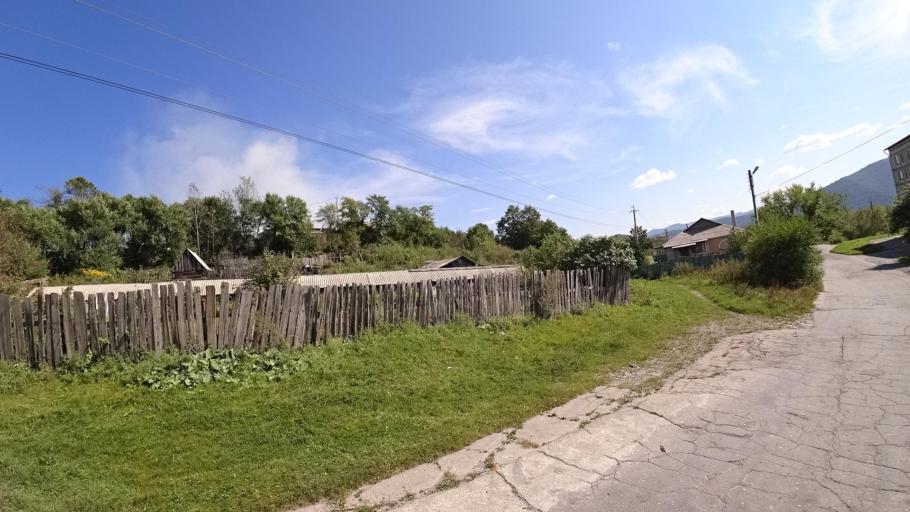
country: RU
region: Jewish Autonomous Oblast
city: Londoko
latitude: 49.0105
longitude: 131.8871
